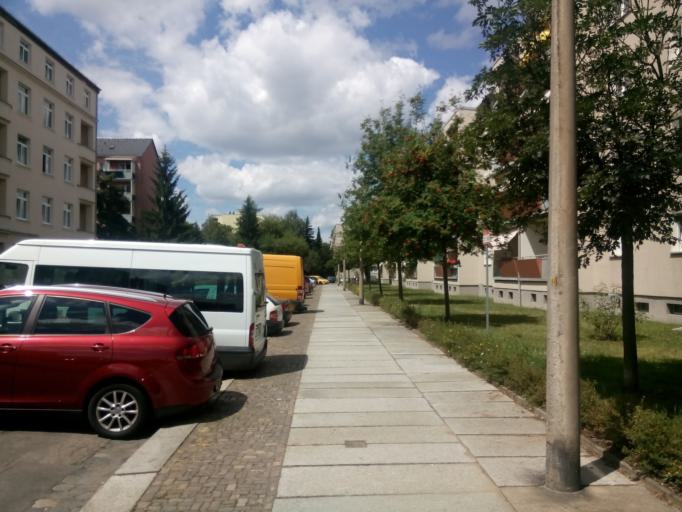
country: DE
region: Saxony
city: Albertstadt
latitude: 51.0443
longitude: 13.7882
